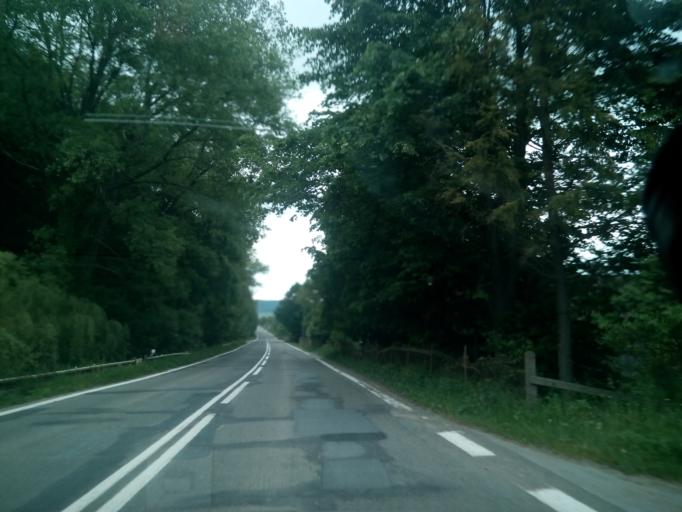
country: SK
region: Kosicky
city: Krompachy
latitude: 48.9958
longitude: 20.8999
